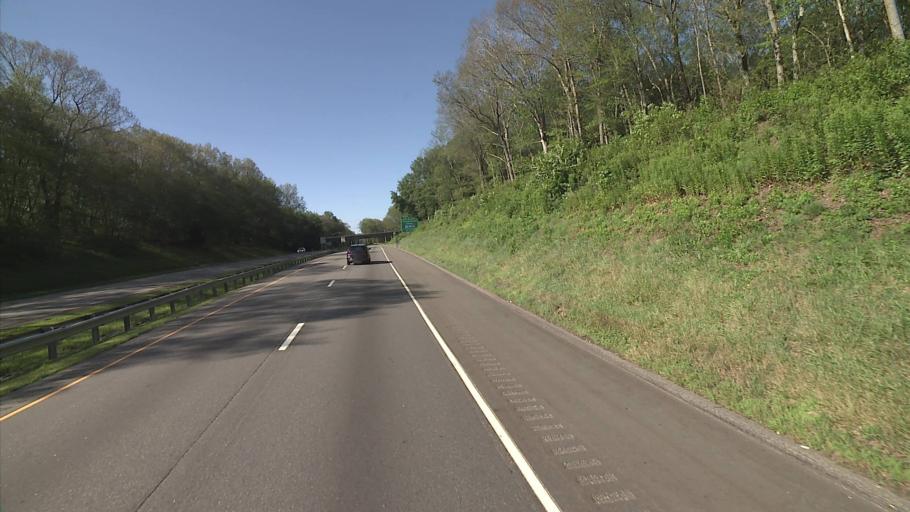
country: US
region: Connecticut
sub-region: New London County
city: Oxoboxo River
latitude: 41.4360
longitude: -72.1196
